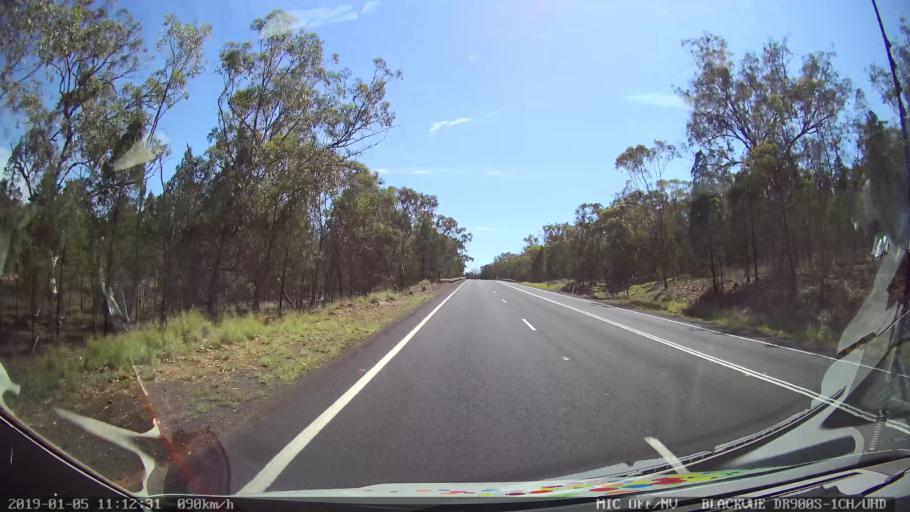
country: AU
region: New South Wales
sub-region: Warrumbungle Shire
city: Coonabarabran
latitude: -31.3812
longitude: 149.2617
